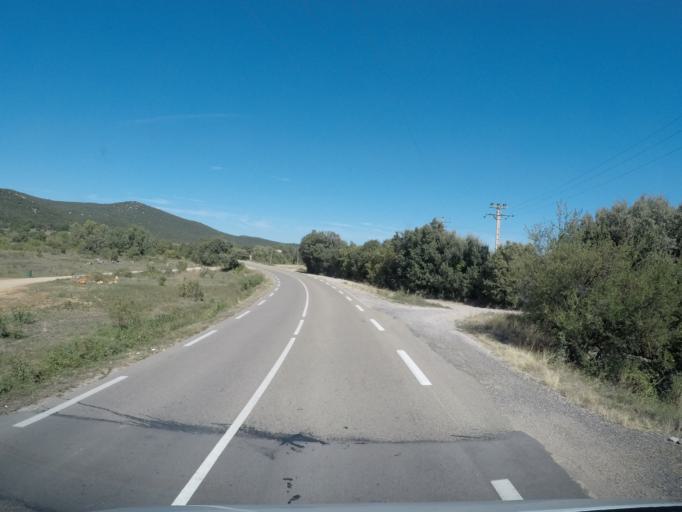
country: FR
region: Languedoc-Roussillon
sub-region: Departement de l'Herault
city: Saint-Martin-de-Londres
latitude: 43.7368
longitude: 3.6927
